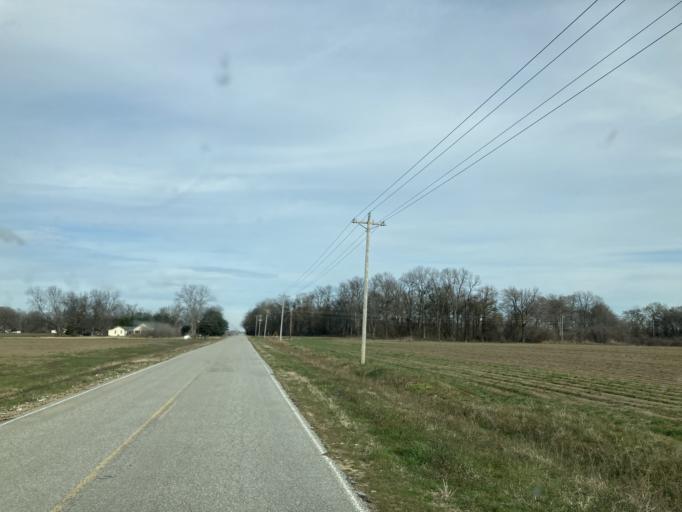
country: US
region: Mississippi
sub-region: Humphreys County
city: Belzoni
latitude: 33.0649
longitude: -90.6155
